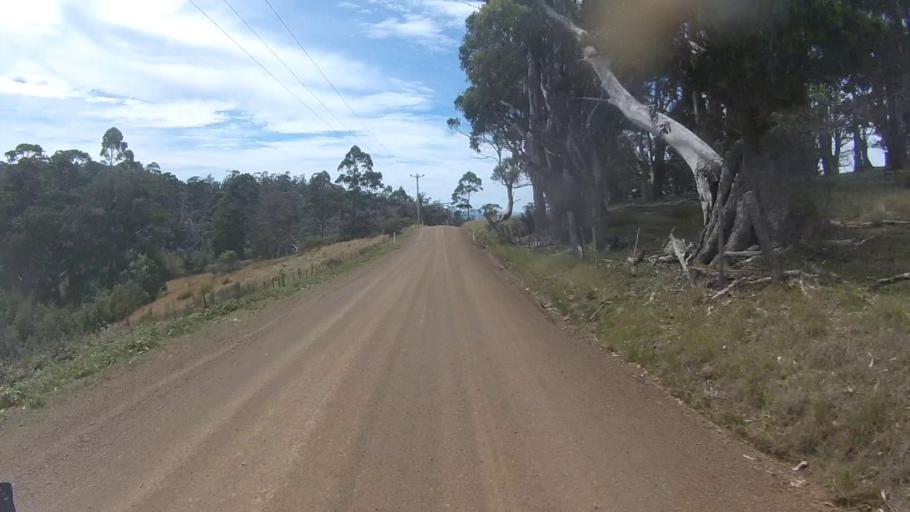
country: AU
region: Tasmania
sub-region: Sorell
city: Sorell
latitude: -42.7887
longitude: 147.8420
